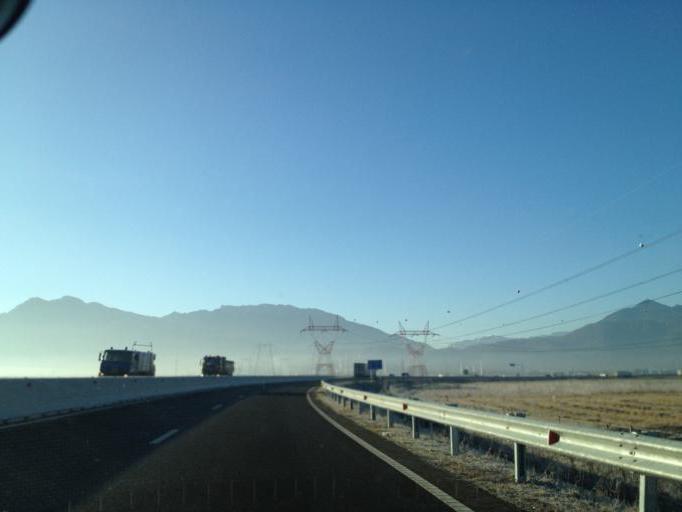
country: RO
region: Brasov
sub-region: Municipiul Sacele
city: Sacele
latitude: 45.6406
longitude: 25.6627
